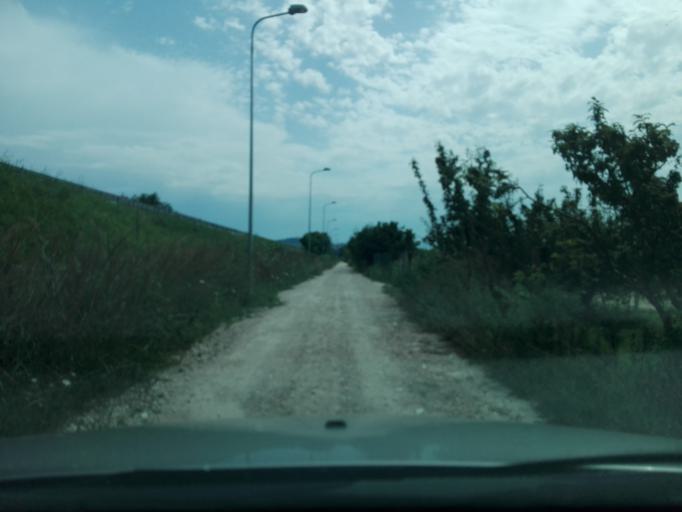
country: IT
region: Abruzzo
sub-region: Provincia di Pescara
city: Cappelle sul Tavo
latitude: 42.4940
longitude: 14.1135
